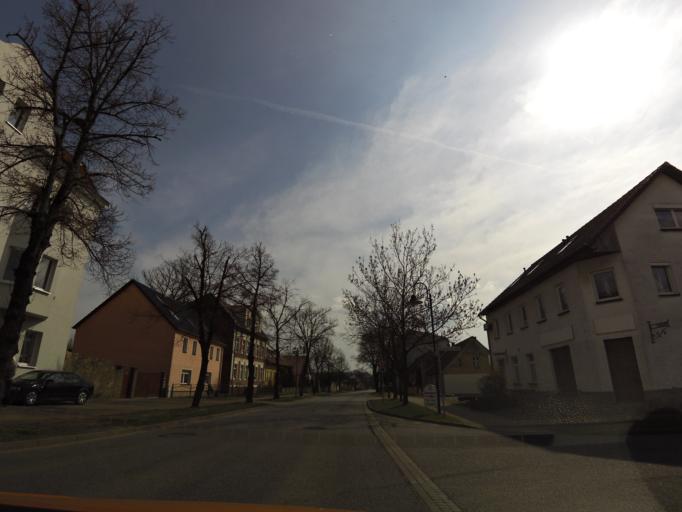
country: DE
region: Brandenburg
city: Rehfelde
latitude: 52.4817
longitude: 13.8526
